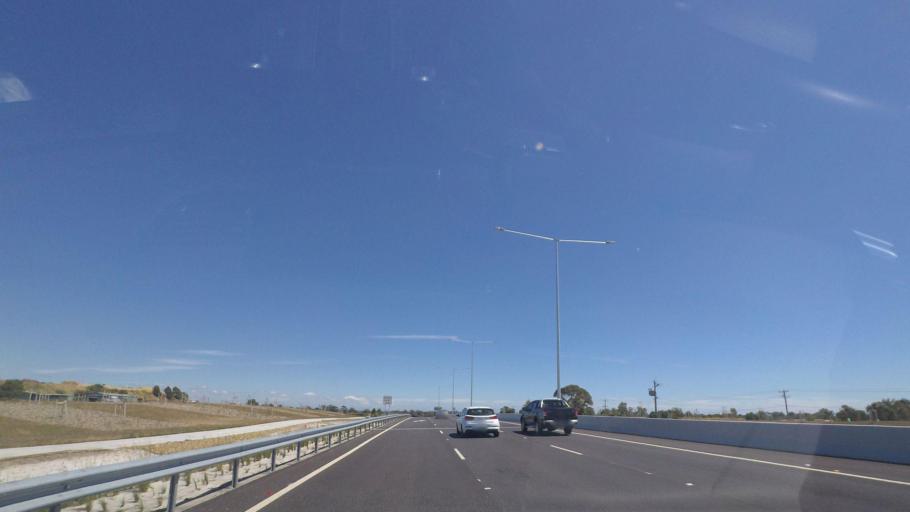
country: AU
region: Victoria
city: Heatherton
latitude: -37.9623
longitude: 145.1182
